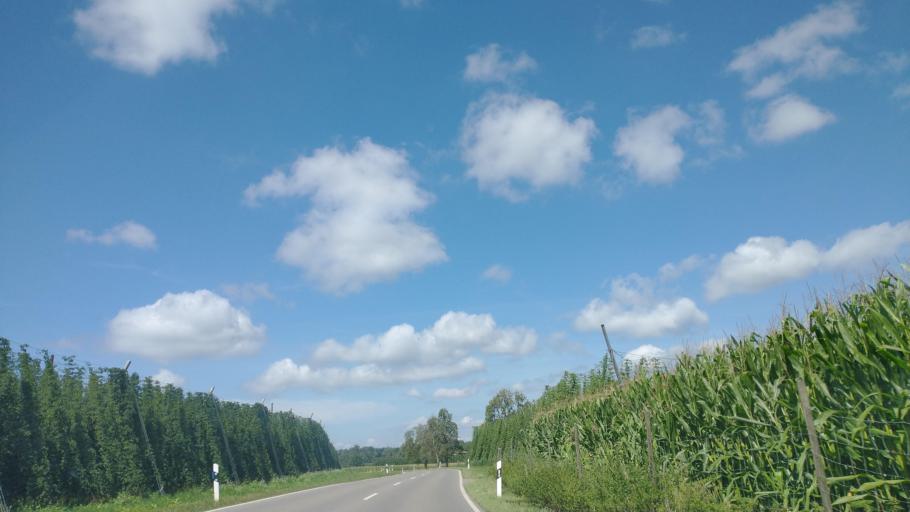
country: DE
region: Baden-Wuerttemberg
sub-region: Tuebingen Region
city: Kressbronn am Bodensee
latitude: 47.6254
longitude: 9.6102
